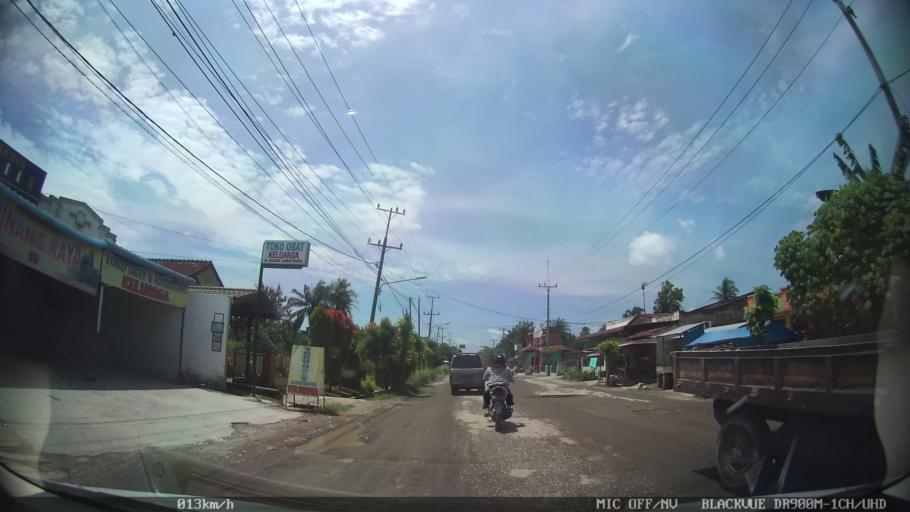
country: ID
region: North Sumatra
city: Perbaungan
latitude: 3.5418
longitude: 98.8825
